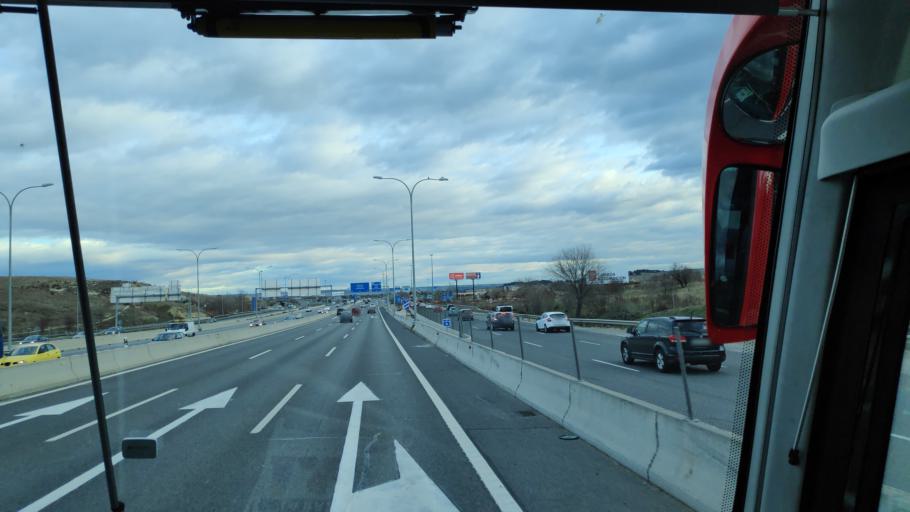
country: ES
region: Madrid
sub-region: Provincia de Madrid
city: Villa de Vallecas
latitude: 40.3651
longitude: -3.5754
